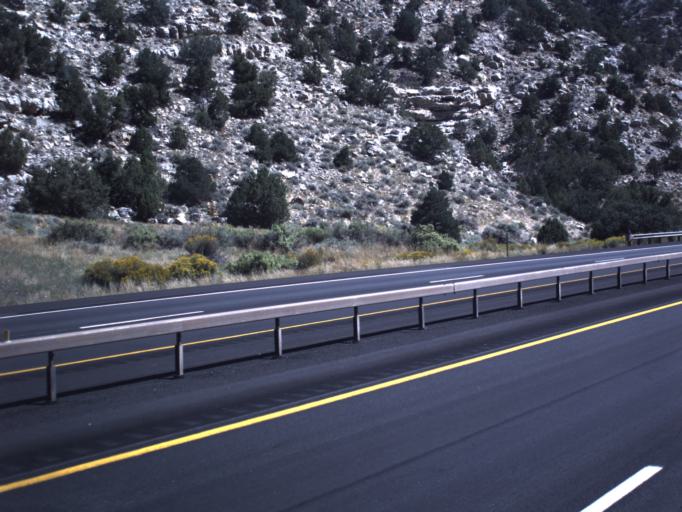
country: US
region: Utah
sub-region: Sevier County
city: Salina
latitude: 38.9009
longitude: -111.6655
